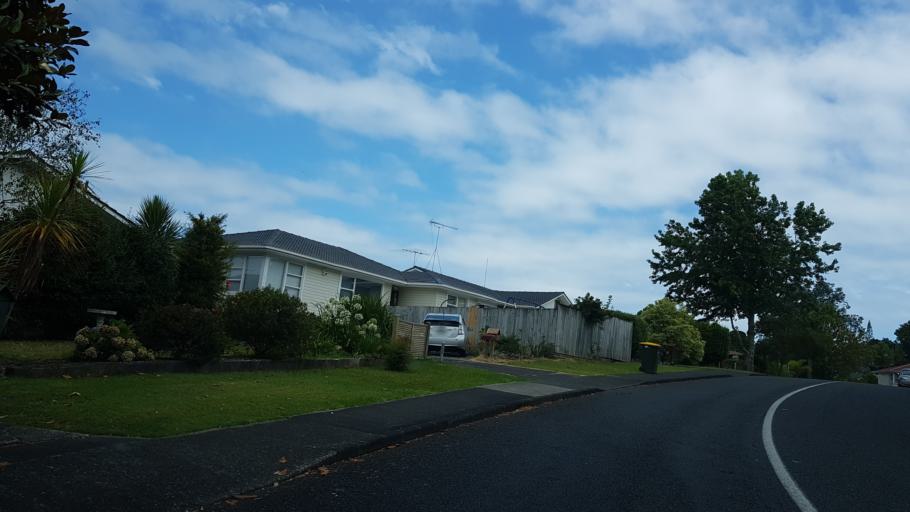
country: NZ
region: Auckland
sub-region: Auckland
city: North Shore
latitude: -36.7743
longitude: 174.7286
